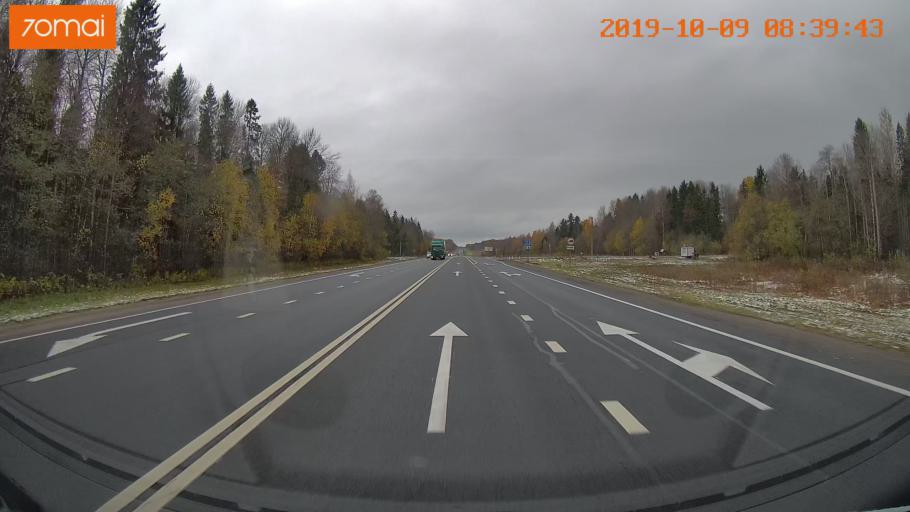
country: RU
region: Vologda
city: Gryazovets
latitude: 58.9758
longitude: 40.1495
